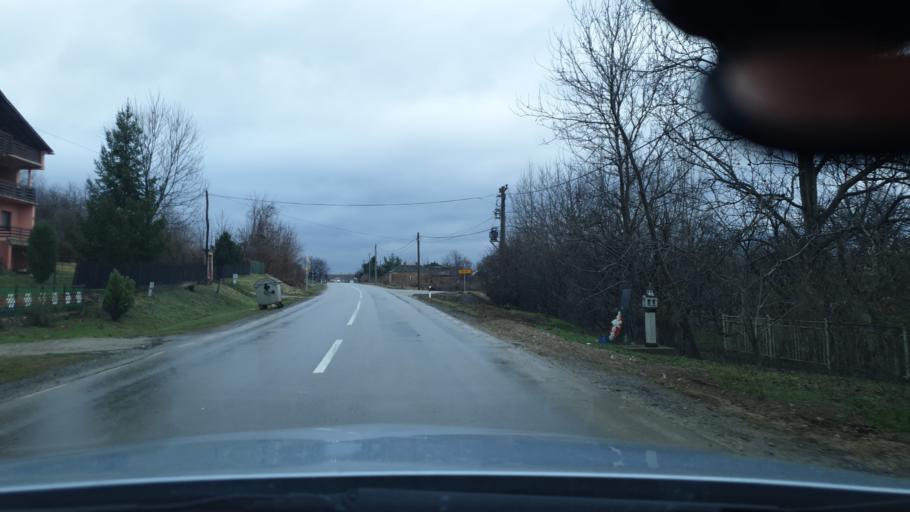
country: RS
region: Central Serbia
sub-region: Branicevski Okrug
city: Petrovac
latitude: 44.4091
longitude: 21.3889
